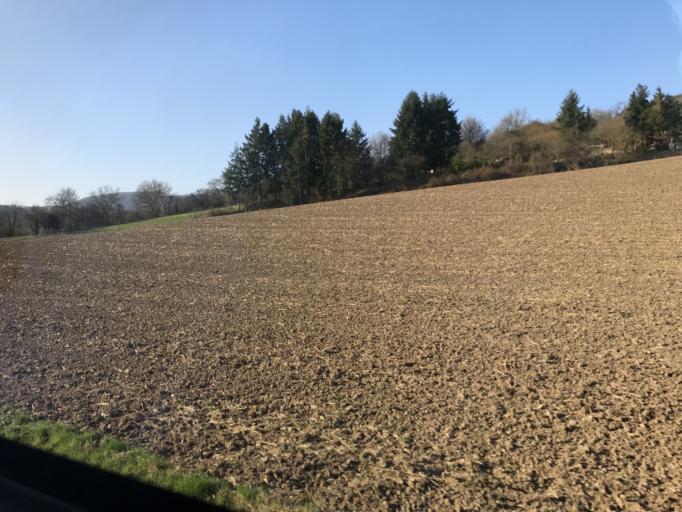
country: DE
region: Rheinland-Pfalz
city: Meisenheim
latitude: 49.7139
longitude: 7.6724
